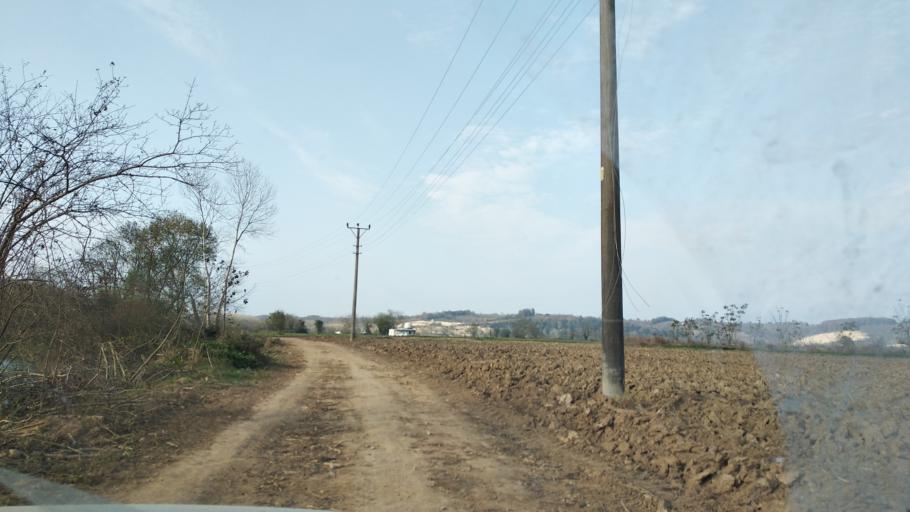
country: TR
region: Sakarya
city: Karasu
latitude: 41.0863
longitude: 30.6014
